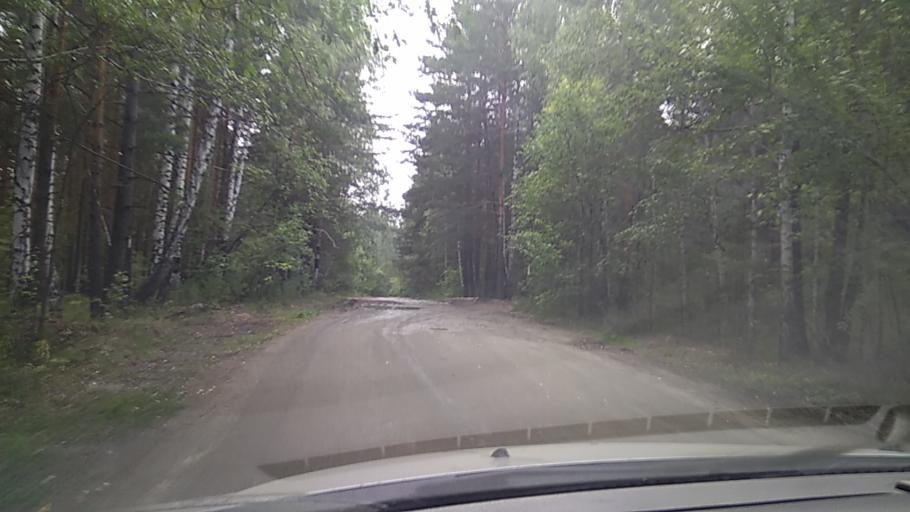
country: RU
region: Chelyabinsk
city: Kyshtym
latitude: 55.6781
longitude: 60.5847
